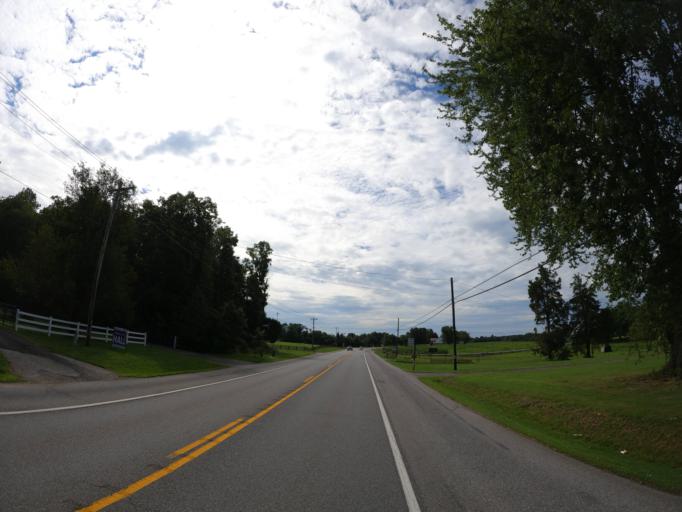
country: US
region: Maryland
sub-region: Saint Mary's County
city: Leonardtown
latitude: 38.3661
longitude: -76.6842
